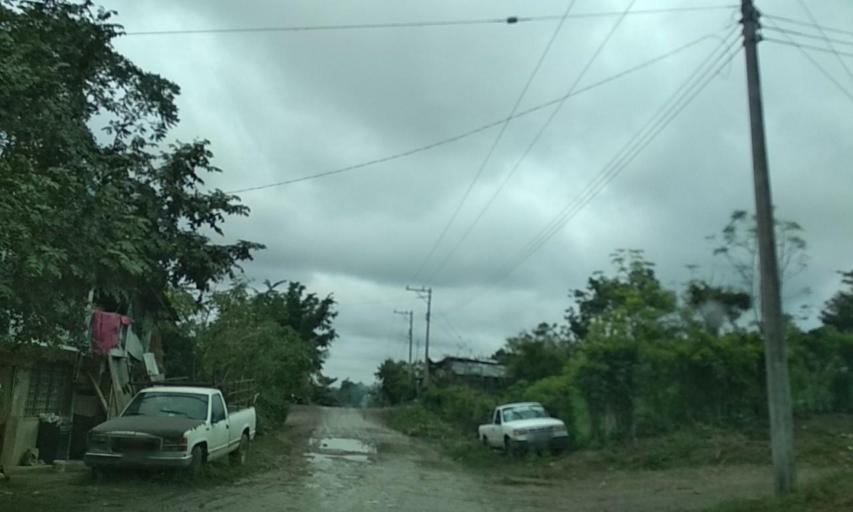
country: MX
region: Puebla
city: Espinal
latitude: 20.3170
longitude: -97.4159
